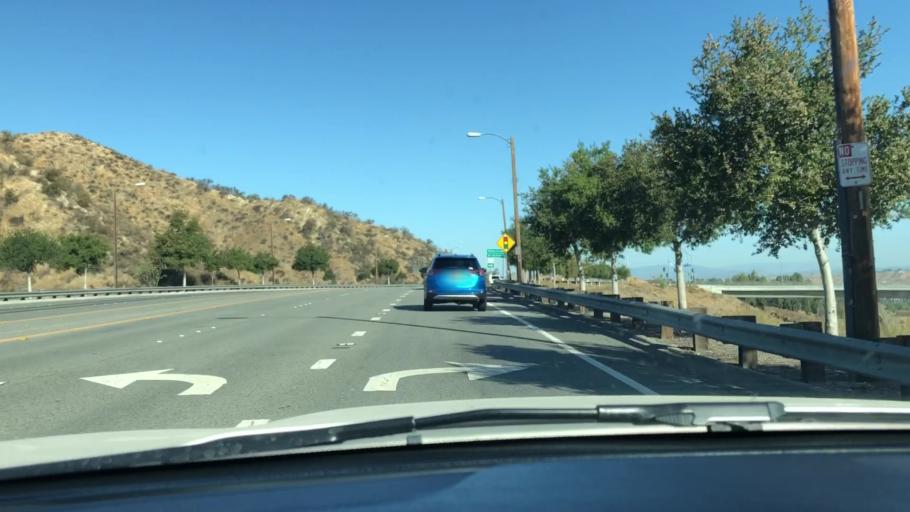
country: US
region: California
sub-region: Los Angeles County
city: Santa Clarita
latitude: 34.4089
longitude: -118.4728
